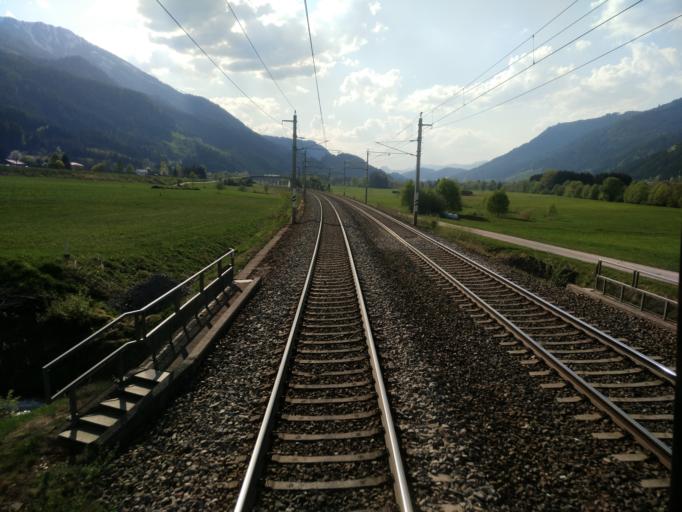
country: AT
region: Styria
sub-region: Politischer Bezirk Liezen
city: Rottenmann
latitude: 47.5154
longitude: 14.4150
